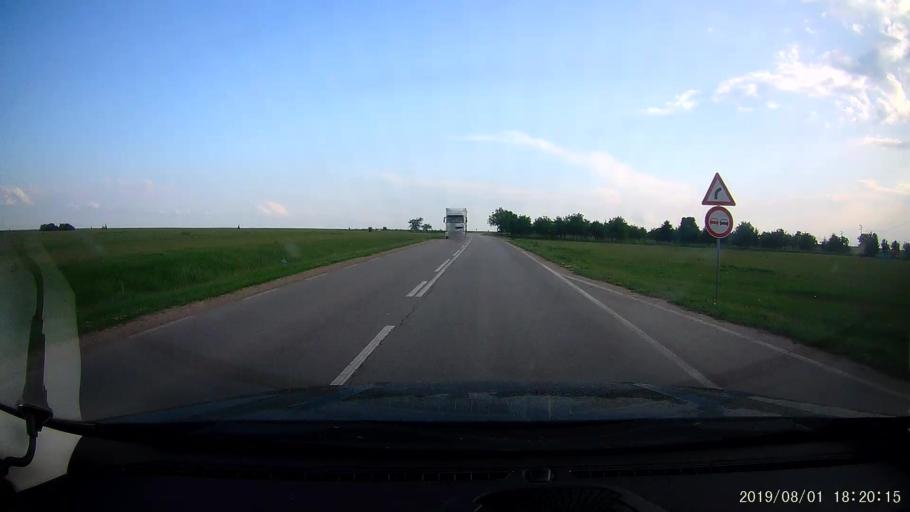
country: BG
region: Shumen
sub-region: Obshtina Kaolinovo
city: Kaolinovo
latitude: 43.6751
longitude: 27.0897
